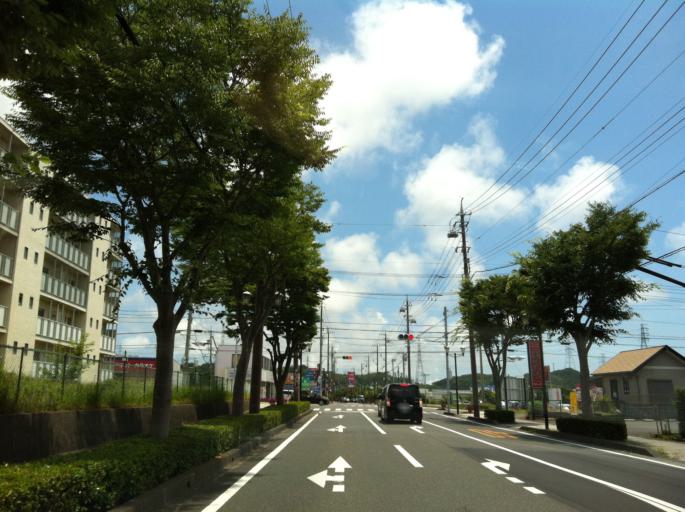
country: JP
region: Shizuoka
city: Sagara
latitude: 34.6379
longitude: 138.1318
